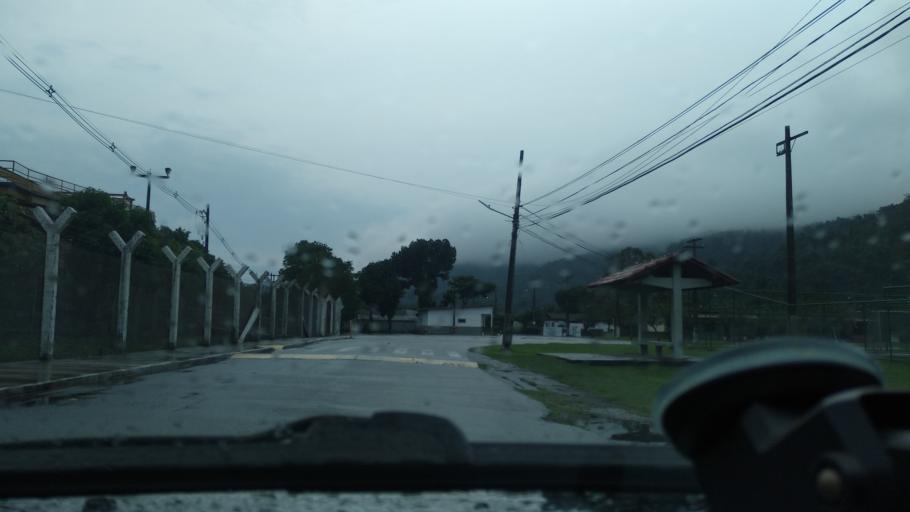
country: BR
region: Rio de Janeiro
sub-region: Angra Dos Reis
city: Angra dos Reis
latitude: -23.0322
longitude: -44.5499
